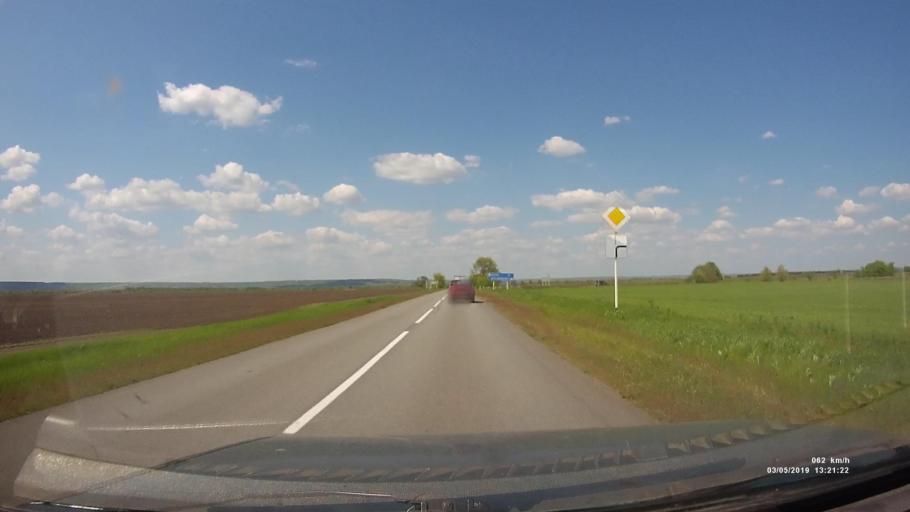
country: RU
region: Rostov
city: Semikarakorsk
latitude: 47.5543
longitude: 40.7475
